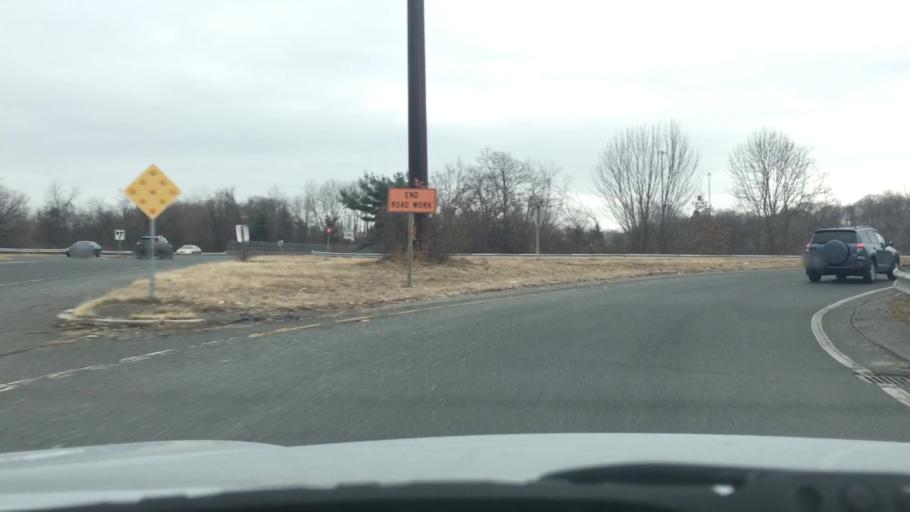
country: US
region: Massachusetts
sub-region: Hampden County
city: North Chicopee
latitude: 42.1822
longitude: -72.6076
